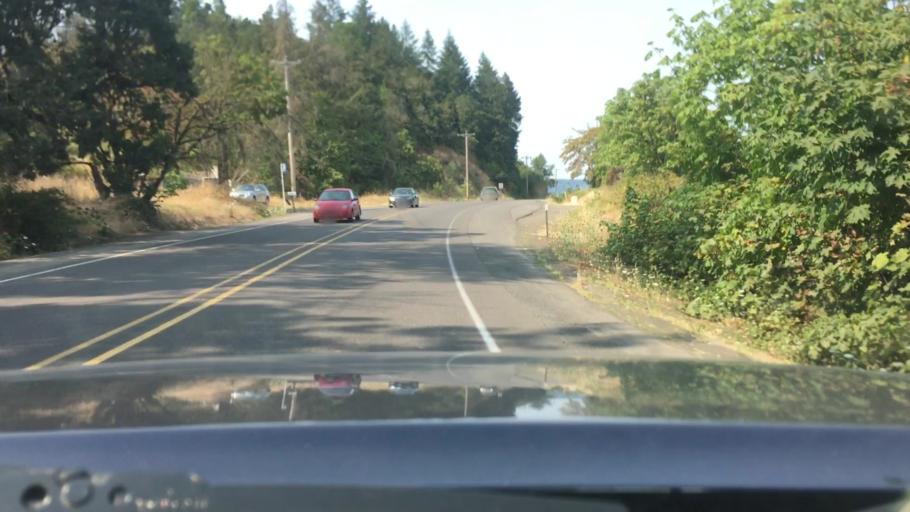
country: US
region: Oregon
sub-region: Lane County
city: Springfield
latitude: 44.0267
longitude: -123.0273
